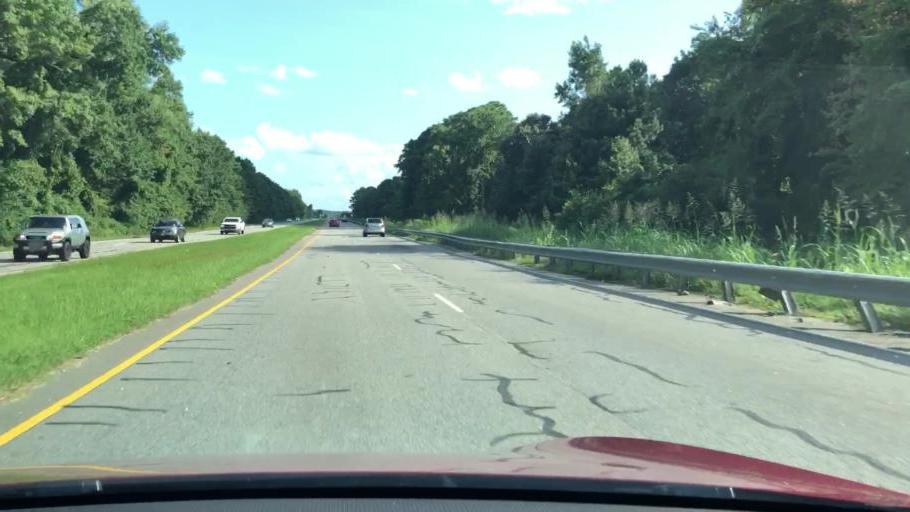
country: US
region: Virginia
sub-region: City of Virginia Beach
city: Virginia Beach
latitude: 36.8350
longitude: -76.0126
